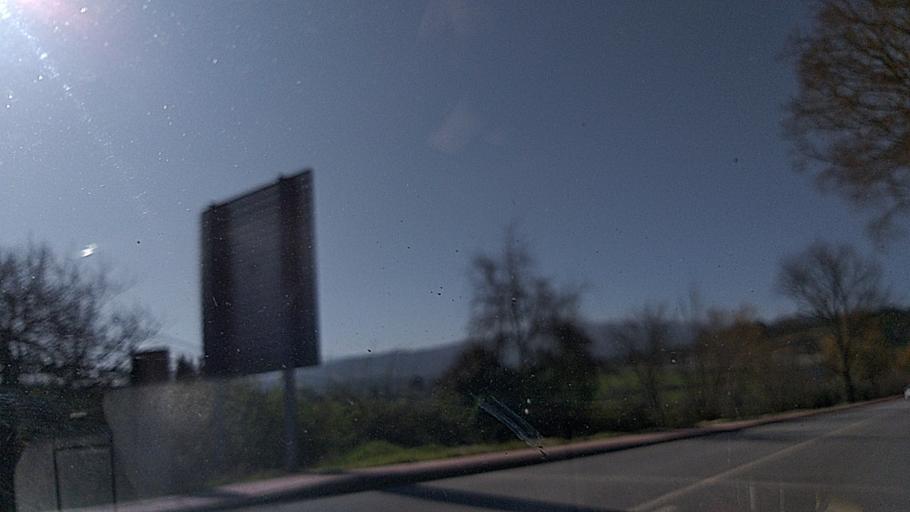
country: PT
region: Guarda
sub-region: Celorico da Beira
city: Celorico da Beira
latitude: 40.6564
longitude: -7.3810
